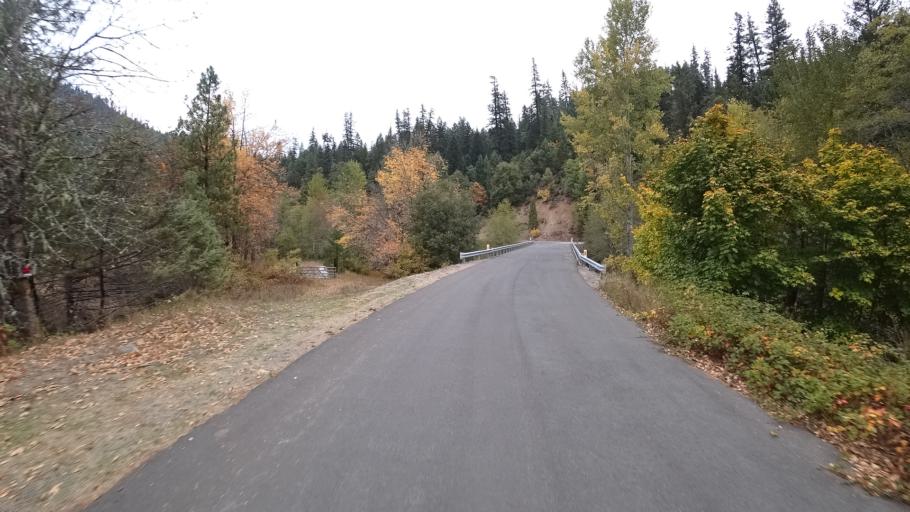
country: US
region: California
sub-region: Siskiyou County
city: Happy Camp
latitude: 41.7488
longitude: -123.3583
